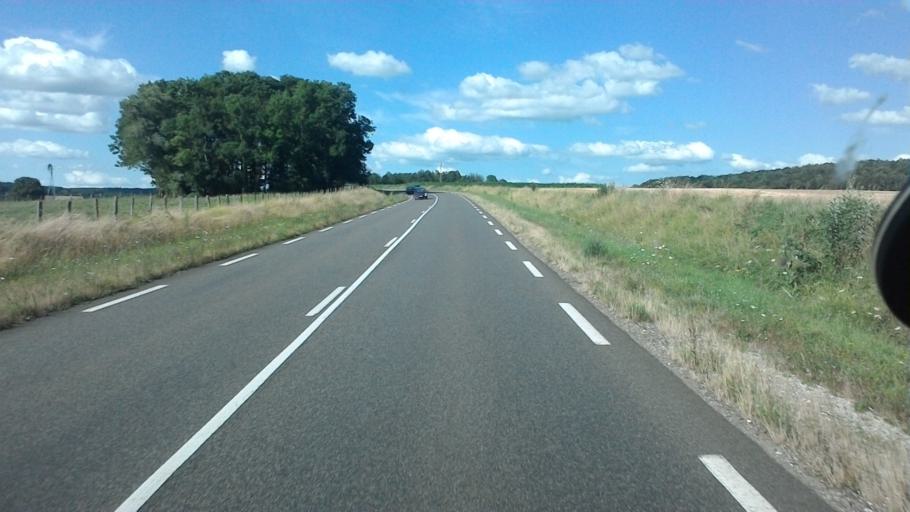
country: FR
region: Franche-Comte
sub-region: Departement de la Haute-Saone
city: Echenoz-la-Meline
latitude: 47.5509
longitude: 6.0626
